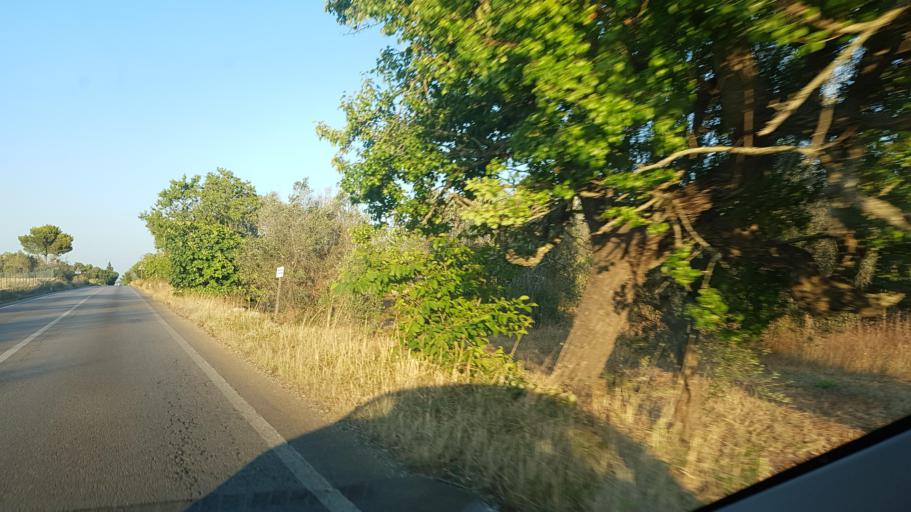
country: IT
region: Apulia
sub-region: Provincia di Lecce
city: Ruffano
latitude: 39.9624
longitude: 18.2700
